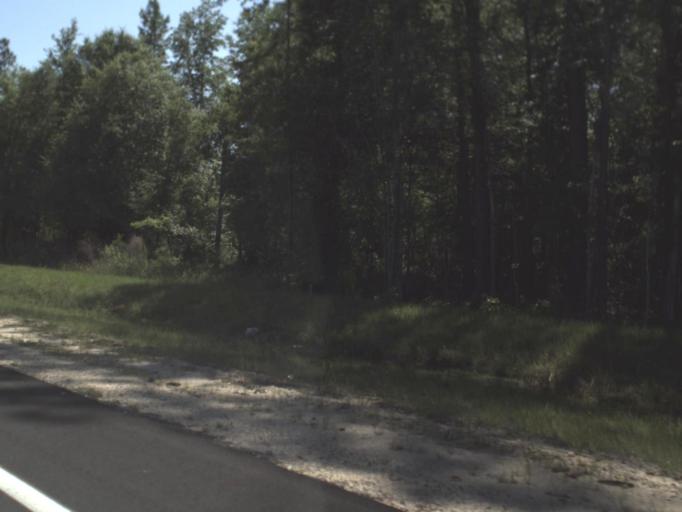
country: US
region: Florida
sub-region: Duval County
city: Baldwin
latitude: 30.3475
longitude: -81.9528
